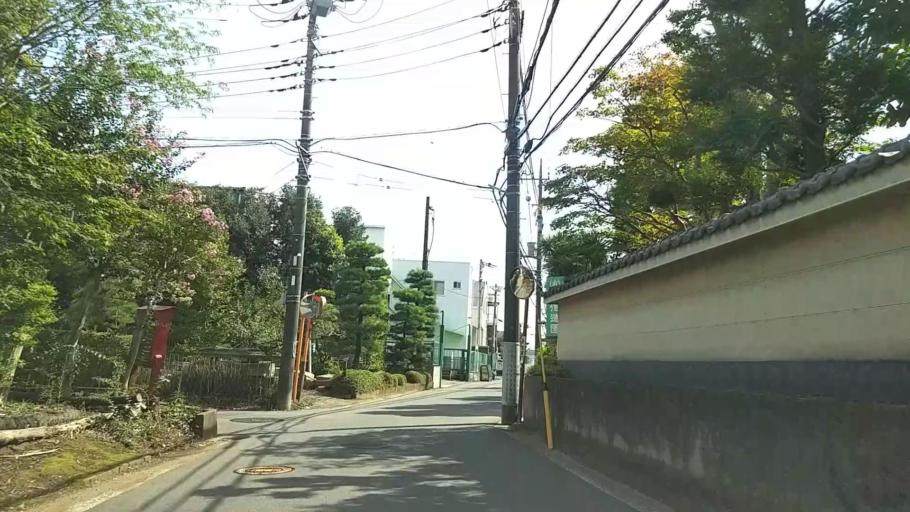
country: JP
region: Kanagawa
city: Yokohama
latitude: 35.5248
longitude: 139.6024
